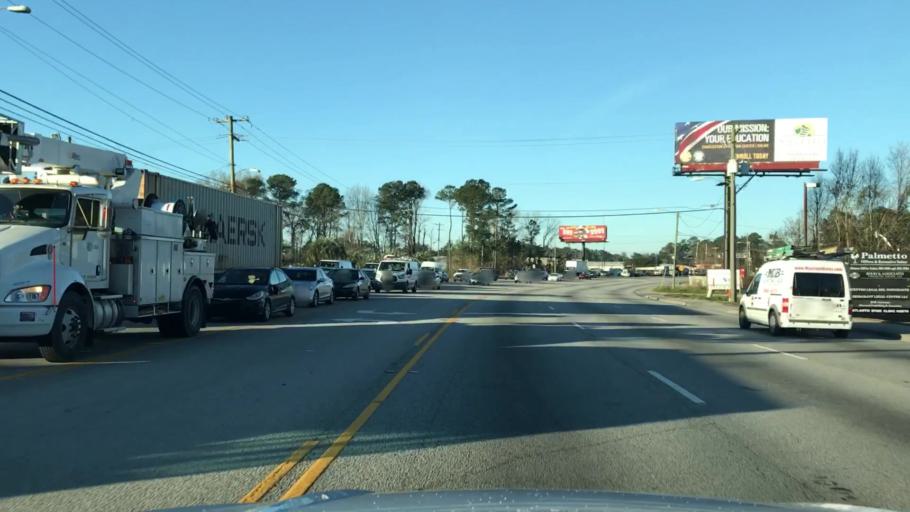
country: US
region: South Carolina
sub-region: Berkeley County
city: Hanahan
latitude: 32.9319
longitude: -80.0563
